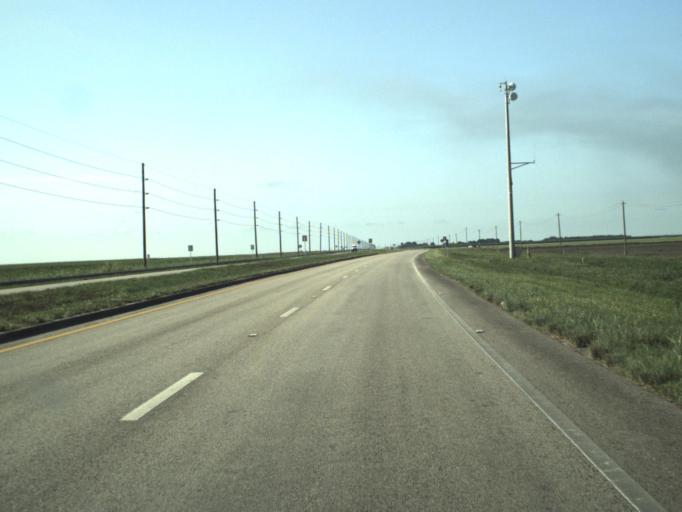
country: US
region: Florida
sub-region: Palm Beach County
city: South Bay
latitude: 26.6439
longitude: -80.7124
